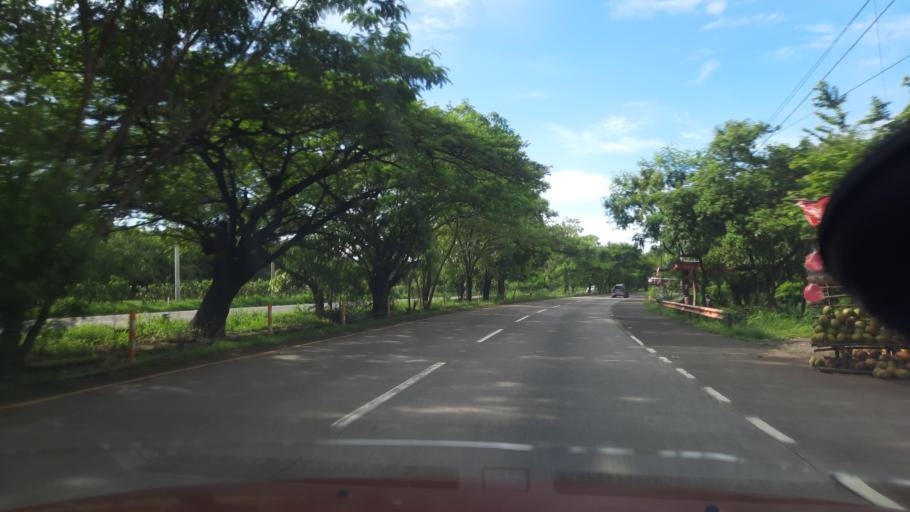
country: SV
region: La Paz
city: El Rosario
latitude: 13.4905
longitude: -89.0673
